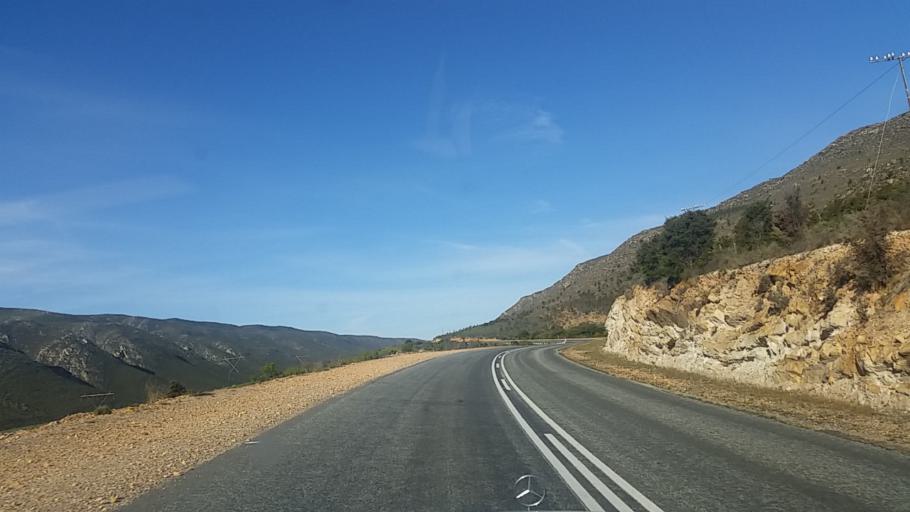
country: ZA
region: Western Cape
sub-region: Eden District Municipality
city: Knysna
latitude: -33.7515
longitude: 22.9588
